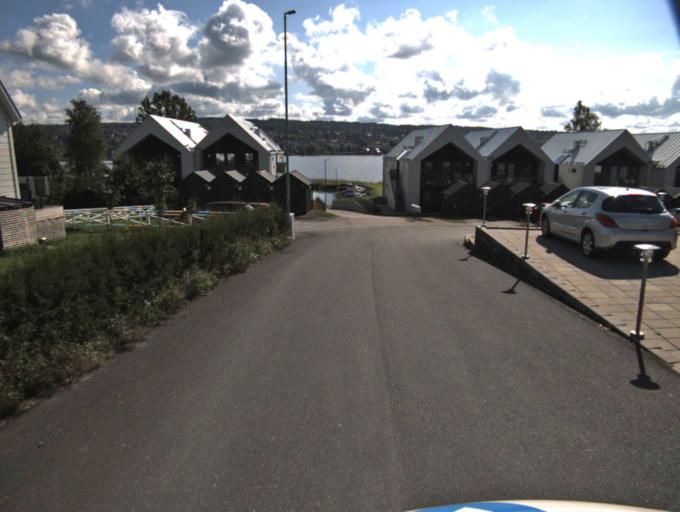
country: SE
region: Vaestra Goetaland
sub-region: Ulricehamns Kommun
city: Ulricehamn
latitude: 57.8001
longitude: 13.3968
